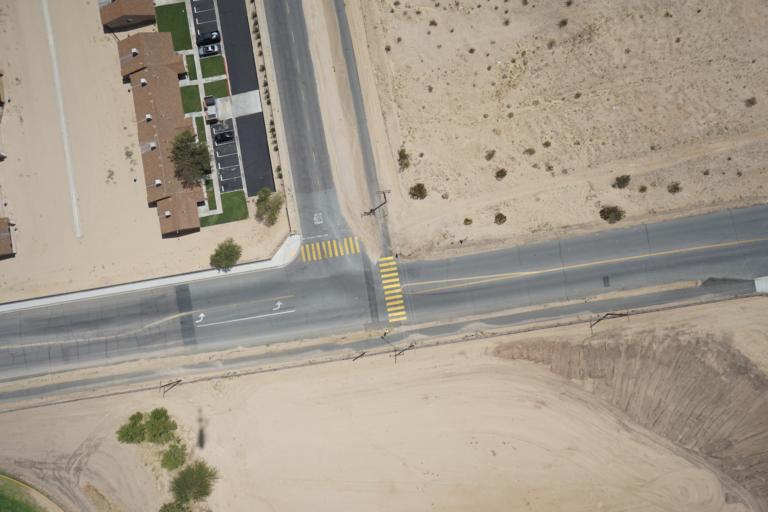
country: US
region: California
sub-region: San Bernardino County
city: Twentynine Palms
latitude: 34.1426
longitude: -116.0719
